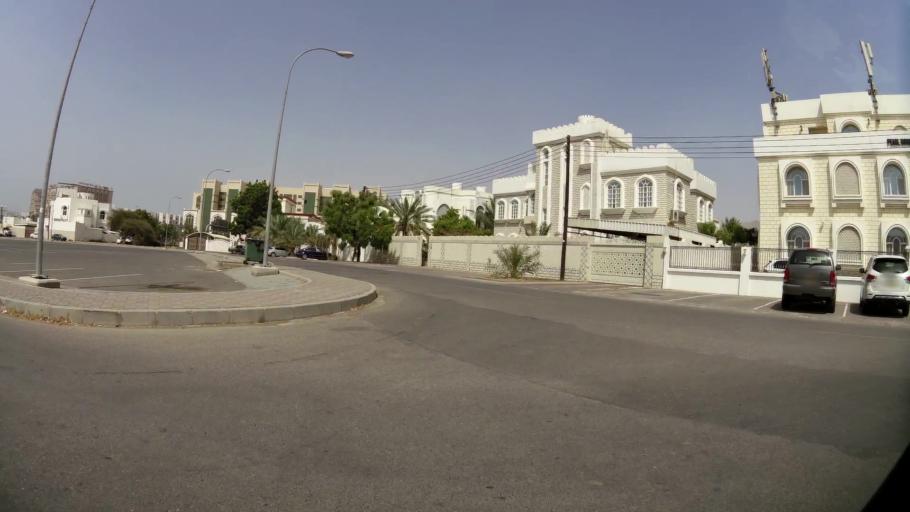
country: OM
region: Muhafazat Masqat
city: Bawshar
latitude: 23.5789
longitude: 58.4061
